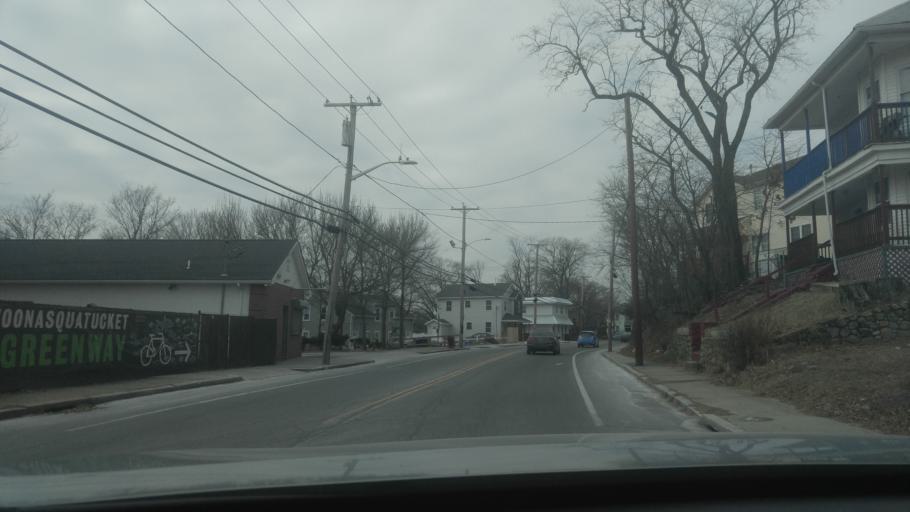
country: US
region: Rhode Island
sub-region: Providence County
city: North Providence
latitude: 41.8263
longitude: -71.4597
